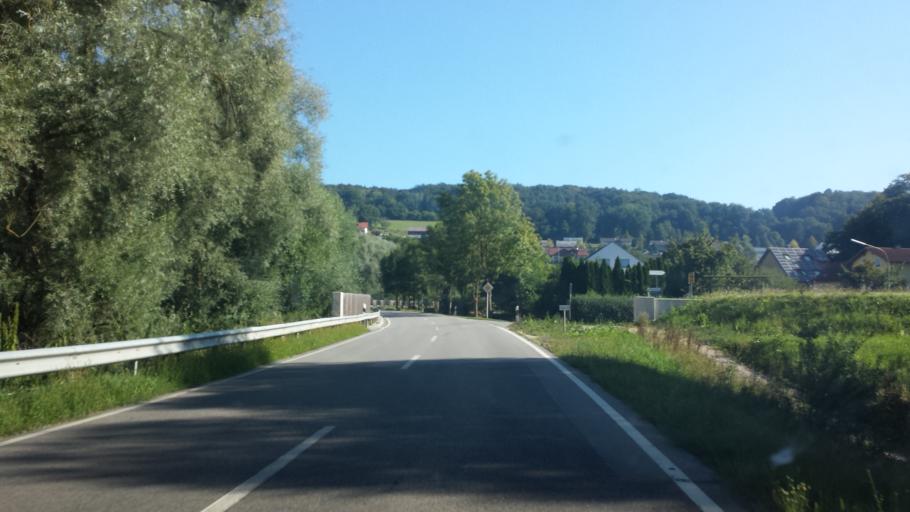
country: DE
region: Bavaria
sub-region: Lower Bavaria
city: Essing
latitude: 48.8885
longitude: 11.8232
